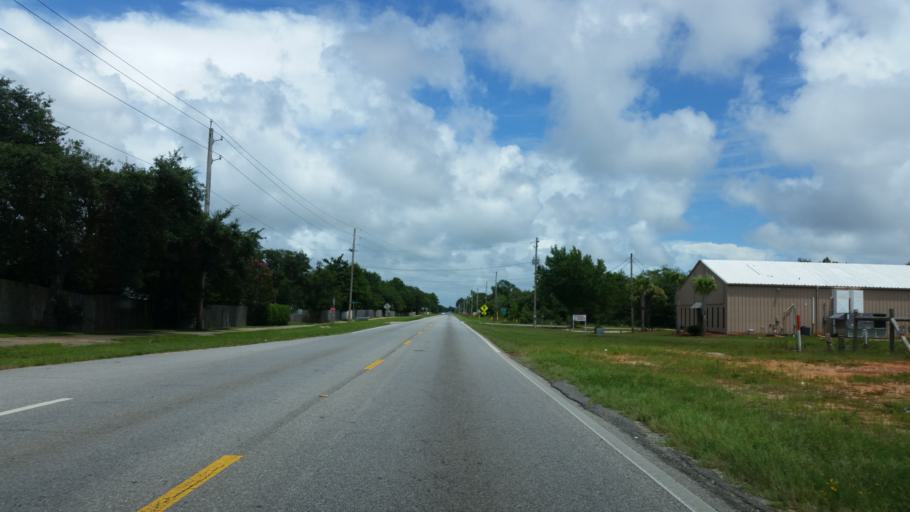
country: US
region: Florida
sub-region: Santa Rosa County
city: Holley
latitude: 30.4326
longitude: -86.8841
